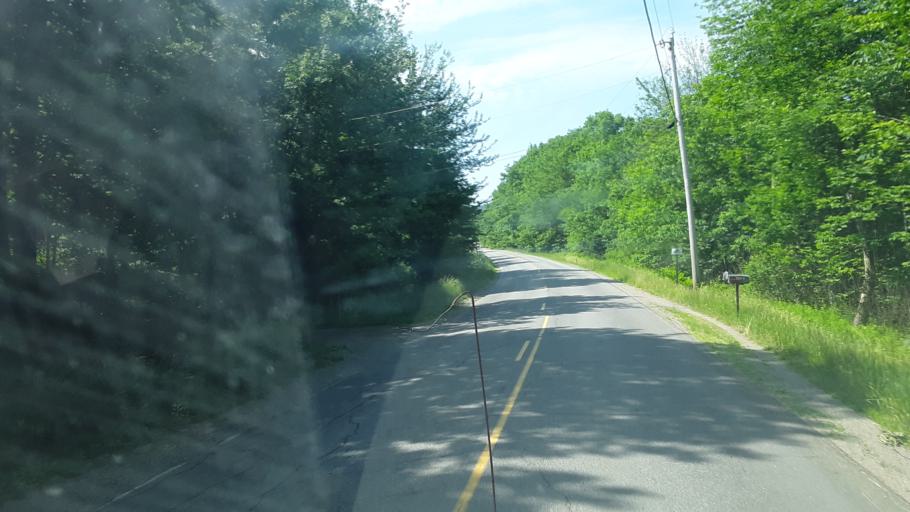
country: US
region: Maine
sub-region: Waldo County
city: Swanville
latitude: 44.5705
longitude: -68.9518
